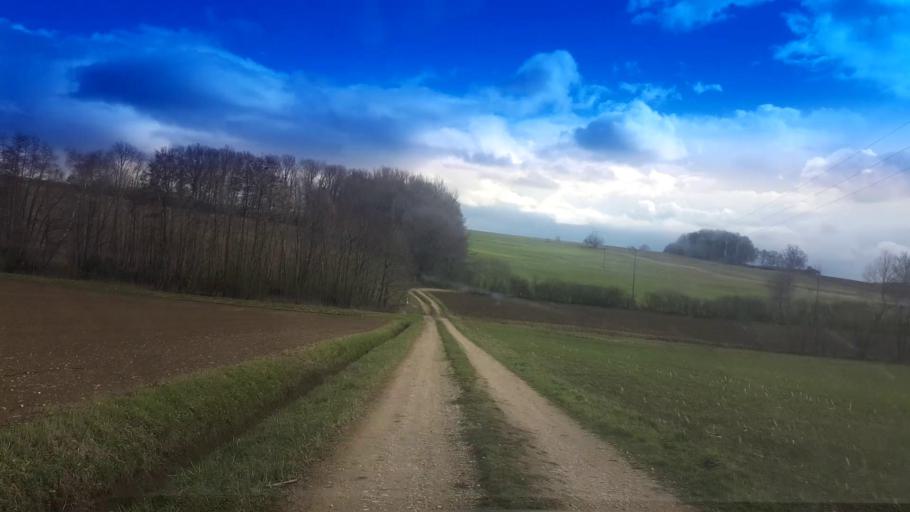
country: DE
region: Bavaria
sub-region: Upper Franconia
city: Schesslitz
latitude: 49.9903
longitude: 11.0183
